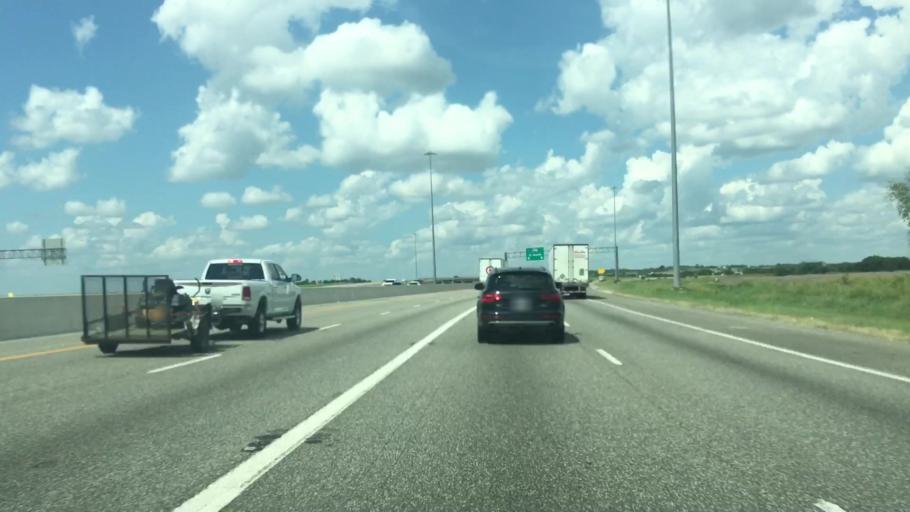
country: US
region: Texas
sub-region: Hill County
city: Hillsboro
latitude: 32.0504
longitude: -97.0942
